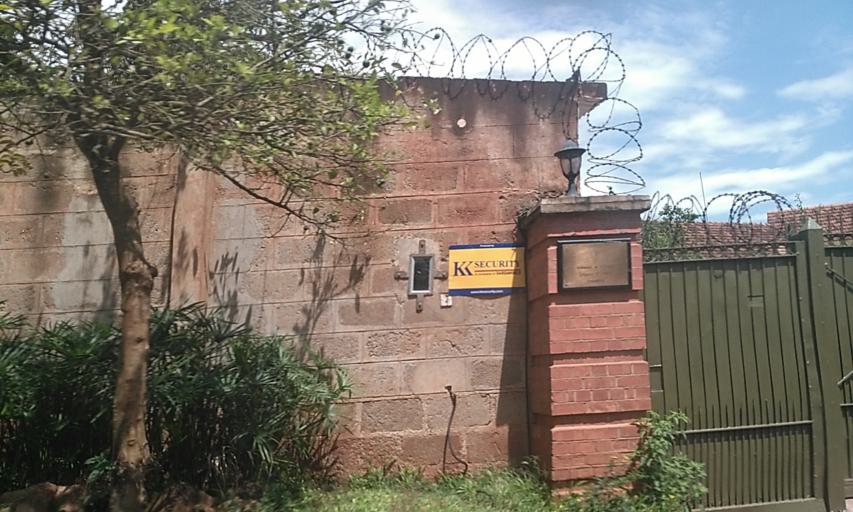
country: UG
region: Central Region
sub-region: Kampala District
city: Kampala
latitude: 0.3313
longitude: 32.5996
